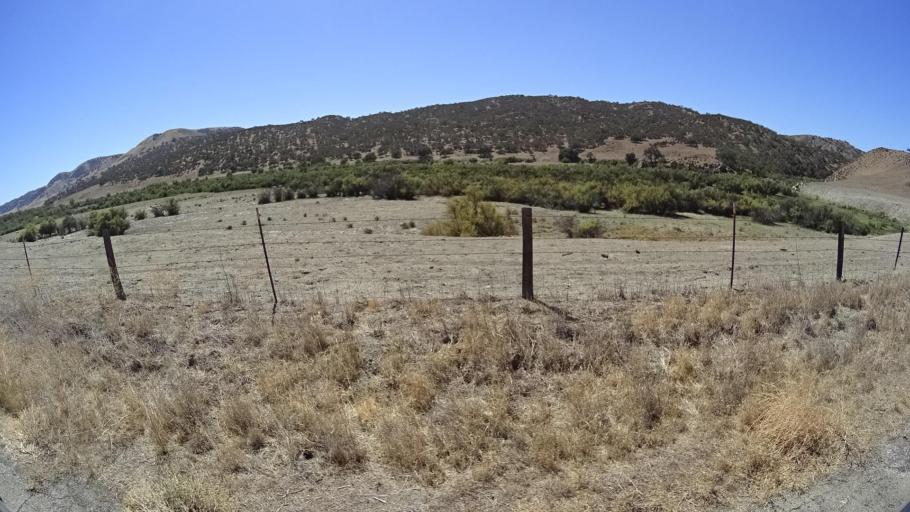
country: US
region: California
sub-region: Monterey County
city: King City
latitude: 36.2925
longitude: -120.9728
